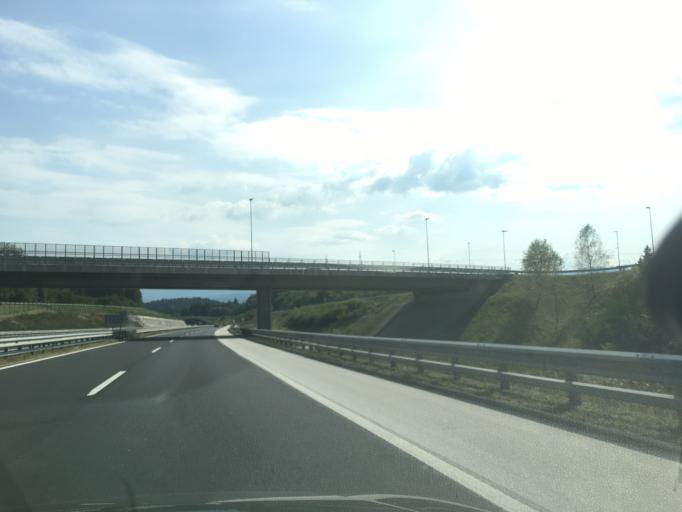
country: SI
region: Novo Mesto
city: Novo Mesto
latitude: 45.8422
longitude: 15.1561
